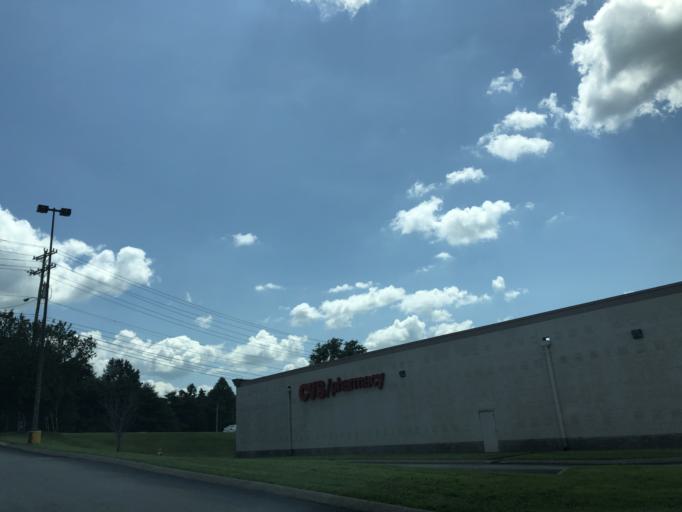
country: US
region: Tennessee
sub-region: Davidson County
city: Lakewood
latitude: 36.2157
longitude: -86.6037
